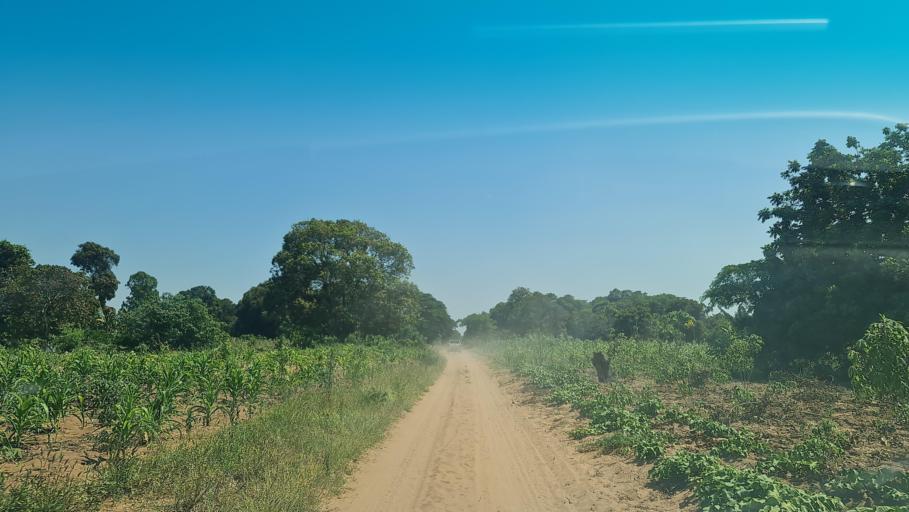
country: MZ
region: Gaza
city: Macia
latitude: -25.0820
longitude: 33.1003
